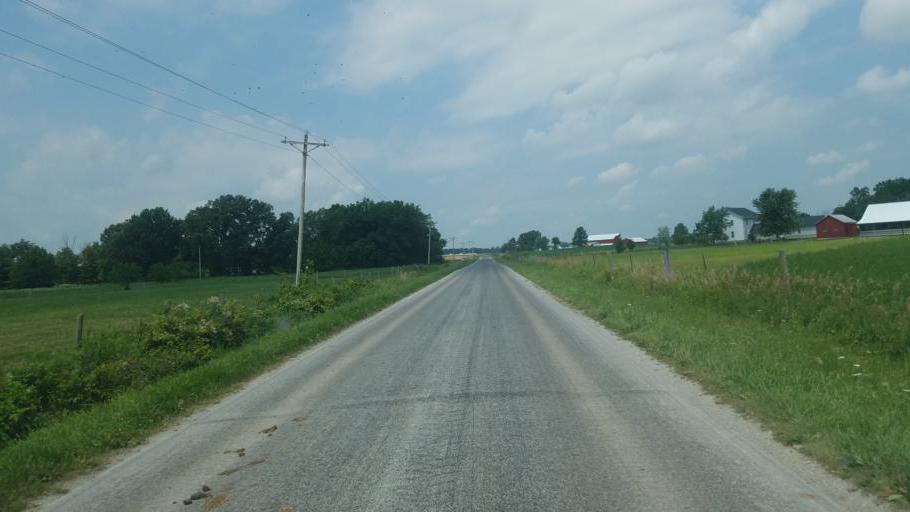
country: US
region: Ohio
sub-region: Hardin County
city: Kenton
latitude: 40.5644
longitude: -83.4456
